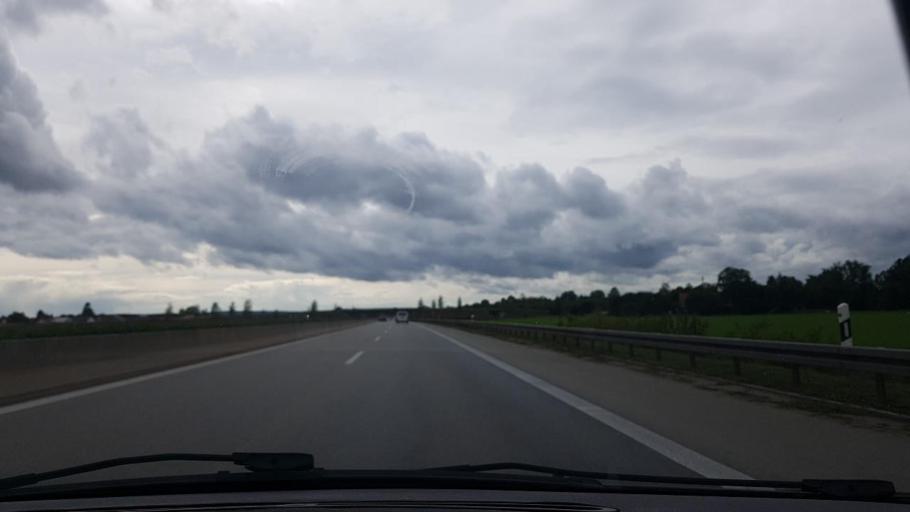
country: DE
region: Bavaria
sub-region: Upper Bavaria
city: Muehldorf
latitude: 48.2761
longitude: 12.5016
